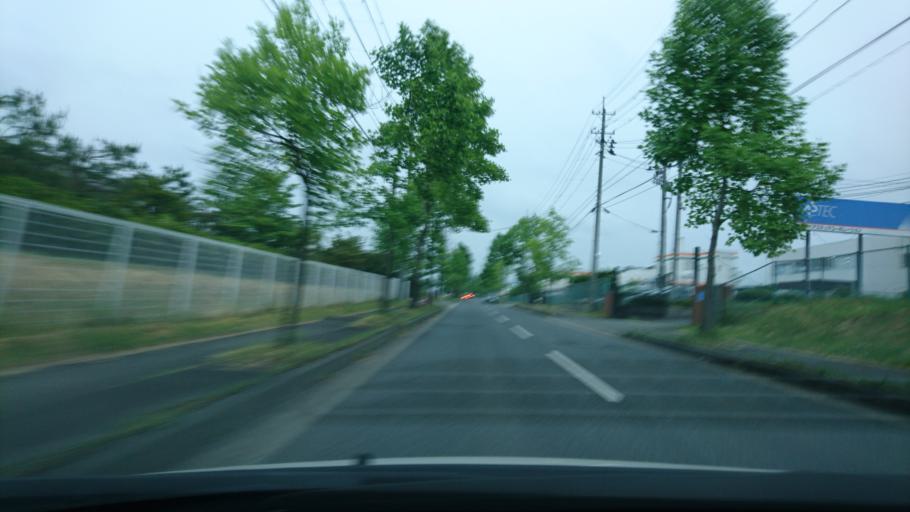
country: JP
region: Iwate
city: Ichinoseki
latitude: 38.9197
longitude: 141.1539
